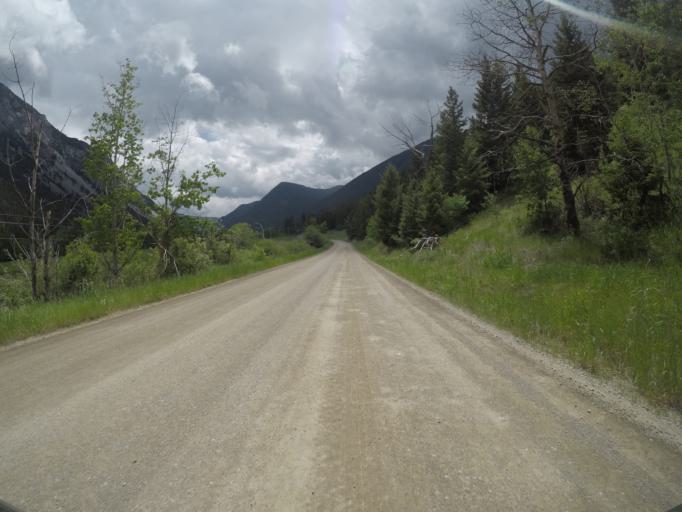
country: US
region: Montana
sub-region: Park County
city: Livingston
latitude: 45.5111
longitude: -110.2272
